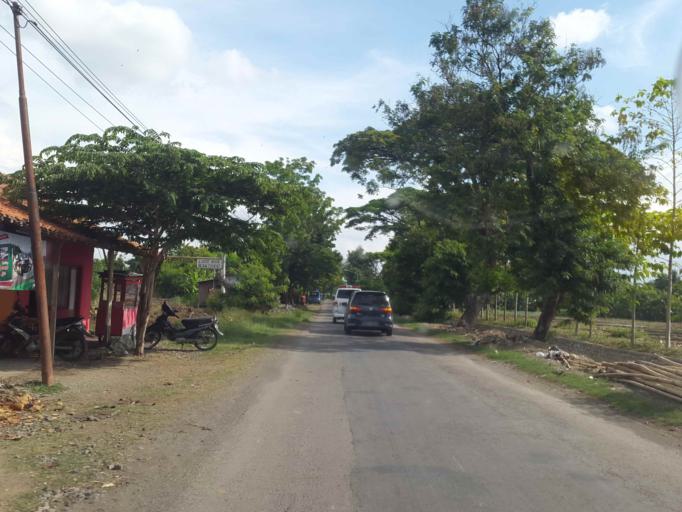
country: ID
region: Central Java
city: Pemalang
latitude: -6.9077
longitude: 109.3274
